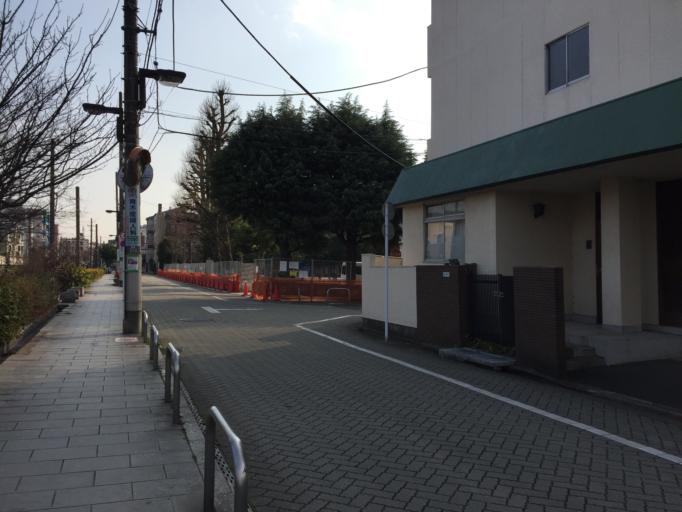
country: JP
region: Tokyo
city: Tokyo
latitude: 35.6618
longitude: 139.6420
